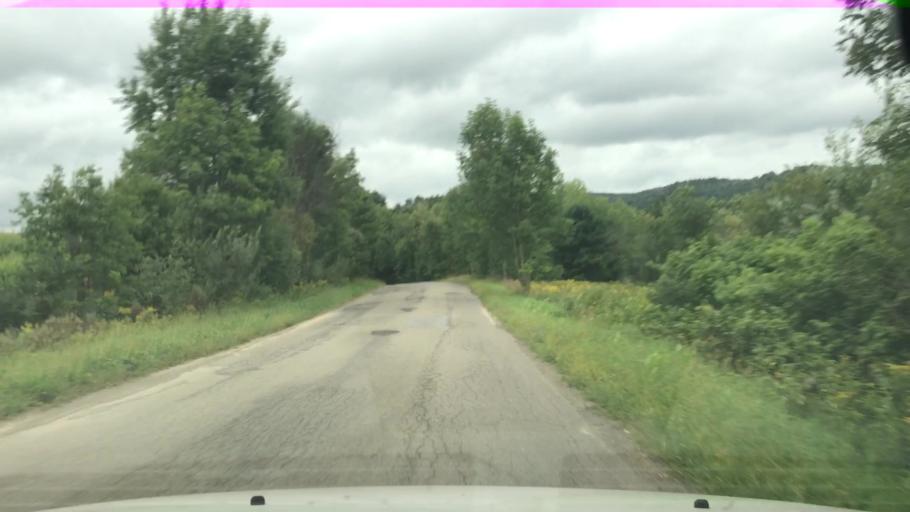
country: US
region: New York
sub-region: Cattaraugus County
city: Little Valley
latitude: 42.3229
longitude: -78.7245
